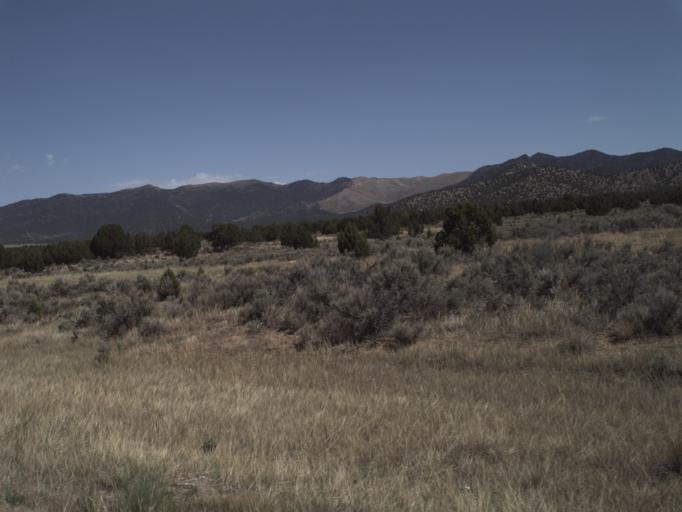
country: US
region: Utah
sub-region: Juab County
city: Mona
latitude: 39.9222
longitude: -112.1507
